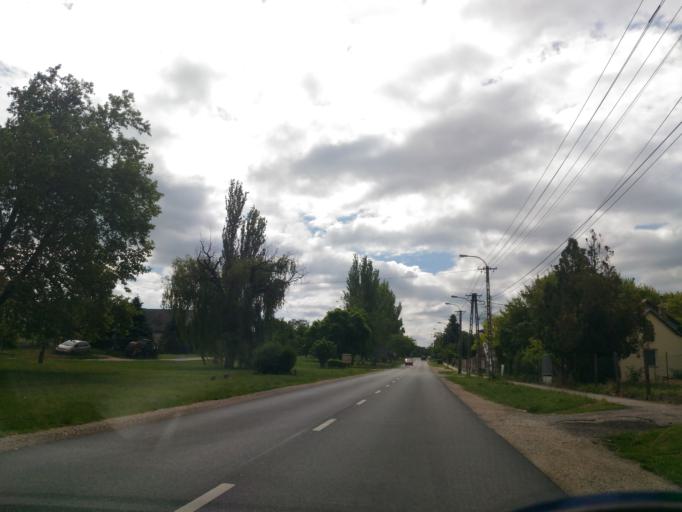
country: HU
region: Fejer
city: Kapolnasnyek
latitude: 47.2250
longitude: 18.6678
